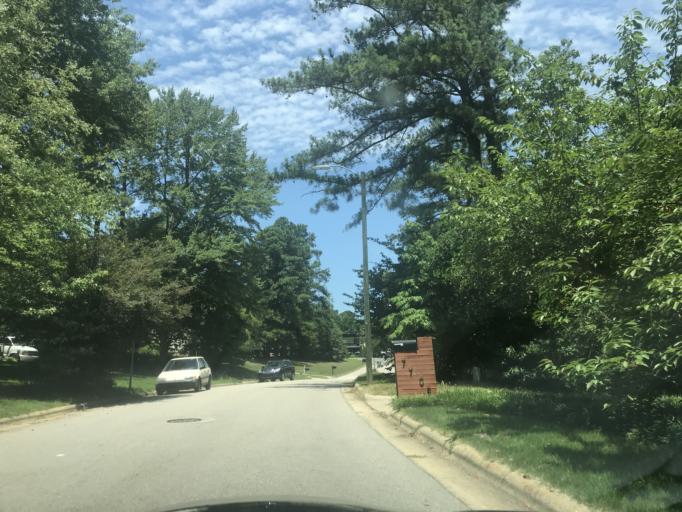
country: US
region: North Carolina
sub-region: Wake County
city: West Raleigh
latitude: 35.8926
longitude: -78.6239
